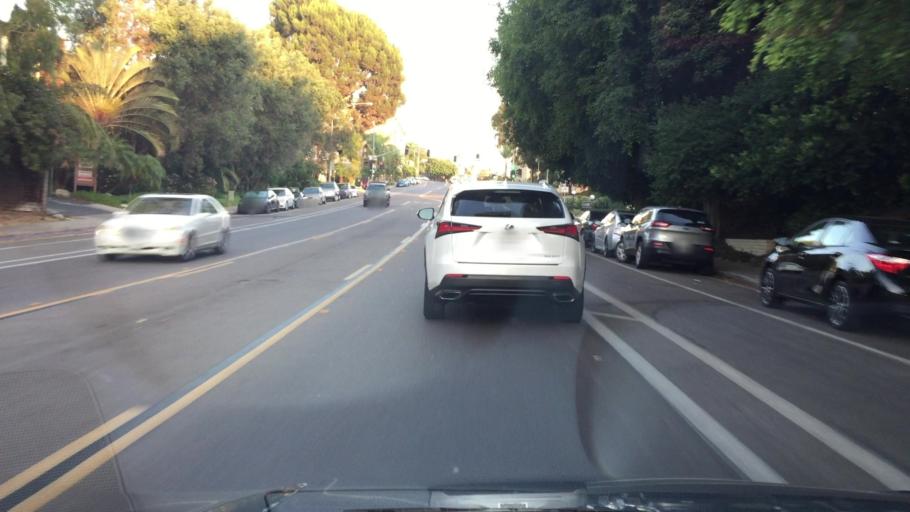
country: US
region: California
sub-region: San Diego County
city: Lemon Grove
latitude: 32.7609
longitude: -117.0819
